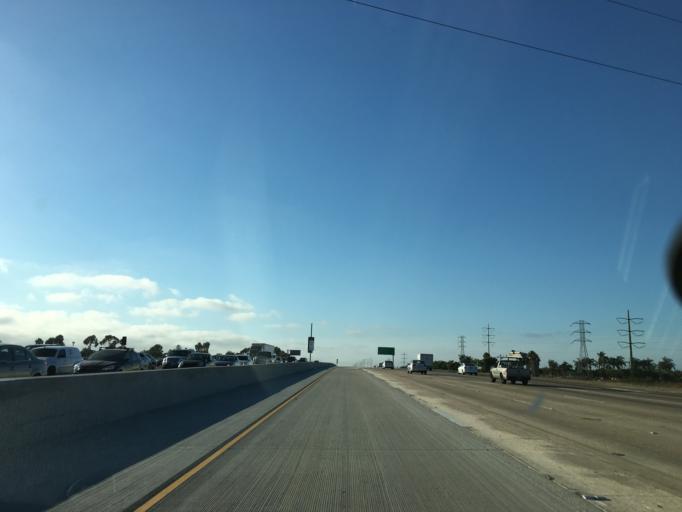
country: US
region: California
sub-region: San Diego County
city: La Jolla
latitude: 32.8555
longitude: -117.1829
